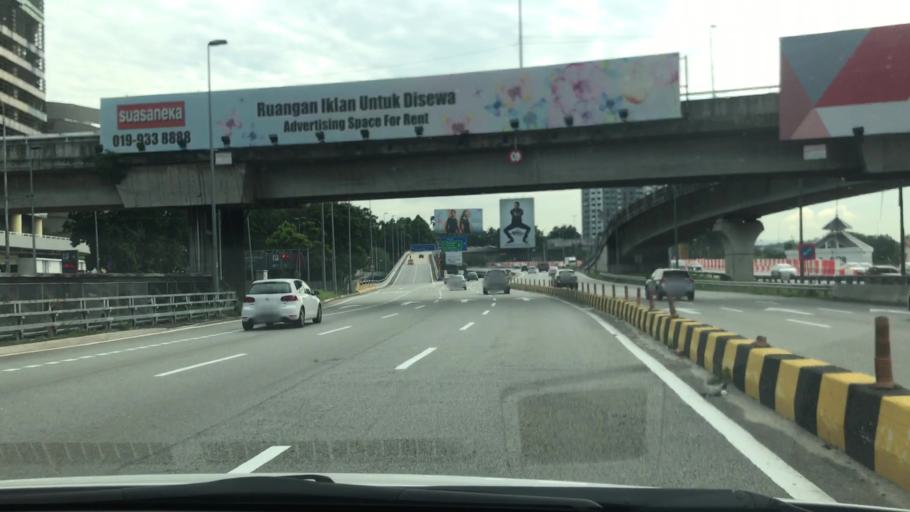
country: MY
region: Kuala Lumpur
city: Kuala Lumpur
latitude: 3.1150
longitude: 101.6749
